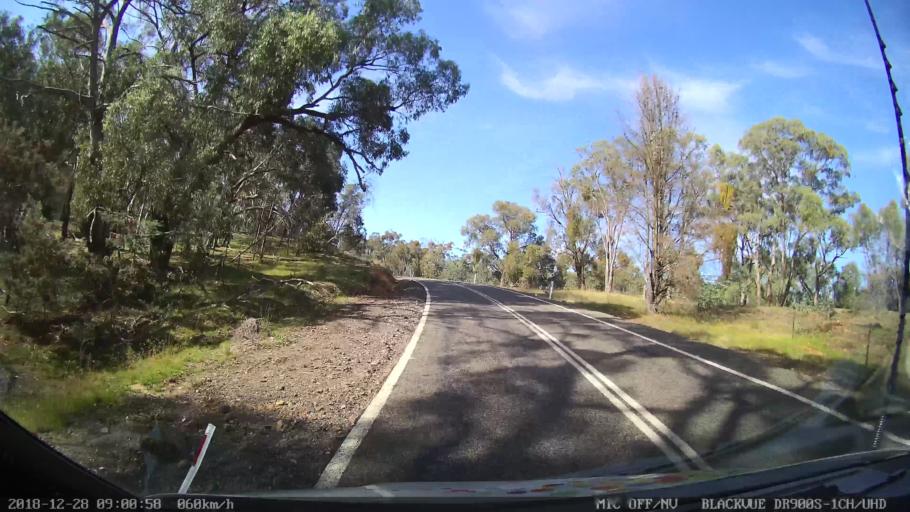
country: AU
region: New South Wales
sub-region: Upper Lachlan Shire
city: Crookwell
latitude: -34.1429
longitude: 149.3338
